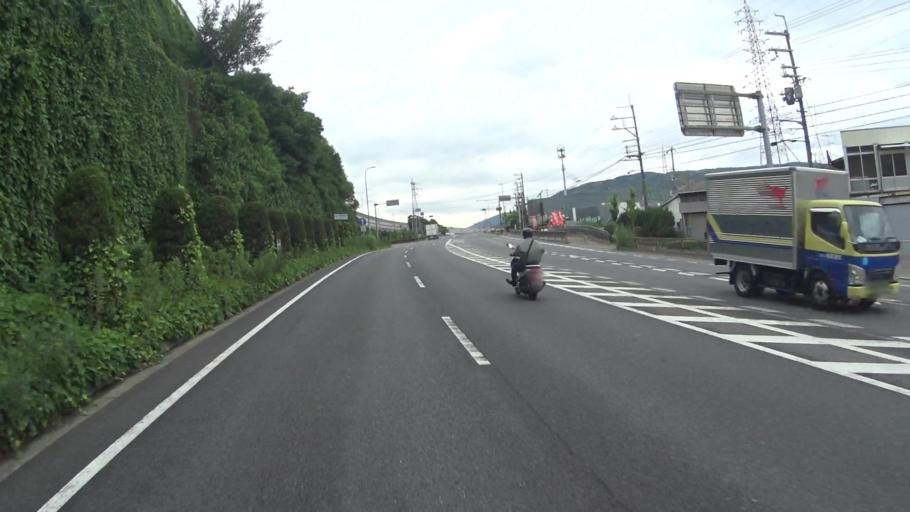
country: JP
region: Kyoto
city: Yawata
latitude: 34.9096
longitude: 135.7044
